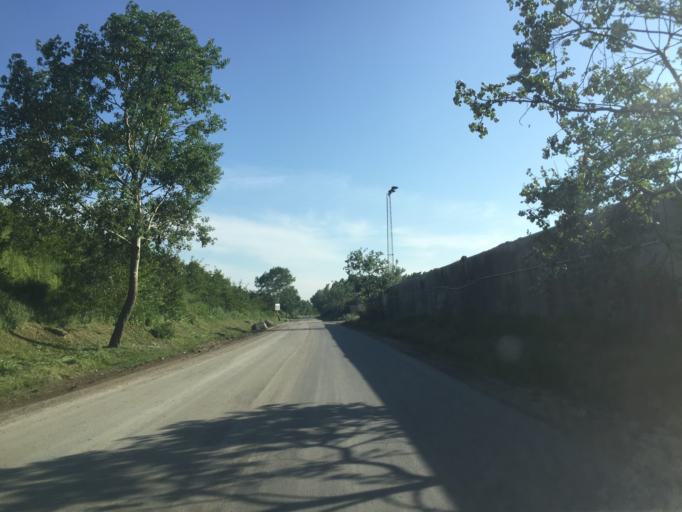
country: DK
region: Capital Region
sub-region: Frederiksberg Kommune
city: Frederiksberg
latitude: 55.6253
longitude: 12.5318
